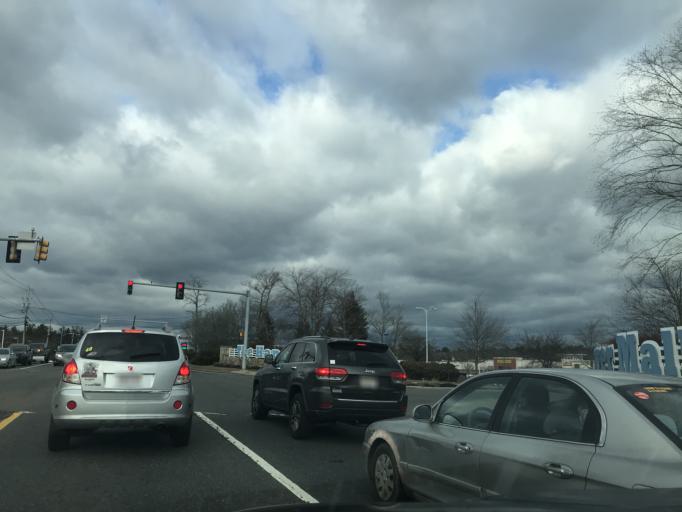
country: US
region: Massachusetts
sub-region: Plymouth County
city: Hanover
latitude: 42.1449
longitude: -70.8446
